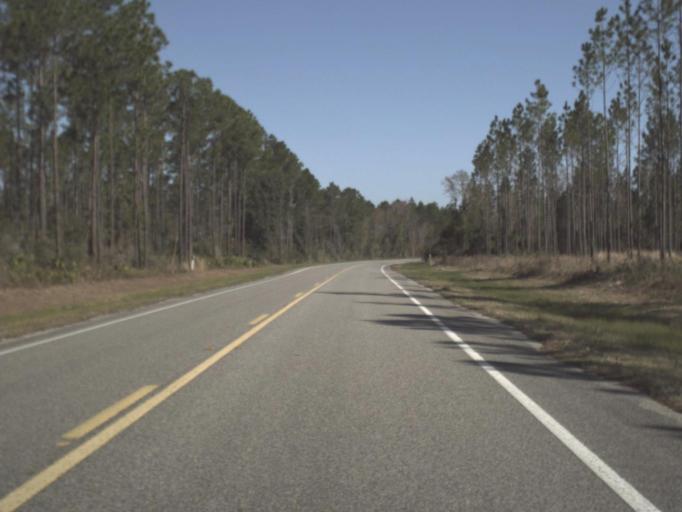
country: US
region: Florida
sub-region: Leon County
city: Woodville
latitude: 30.3064
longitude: -84.0477
